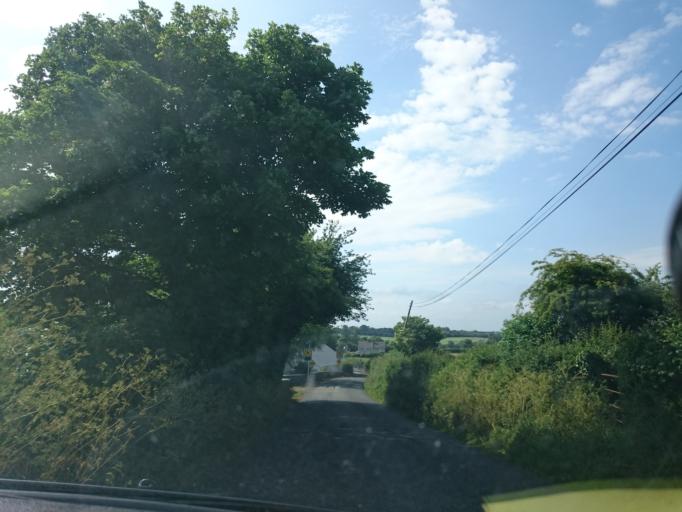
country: IE
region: Leinster
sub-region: Kilkenny
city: Thomastown
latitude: 52.5336
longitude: -7.2210
